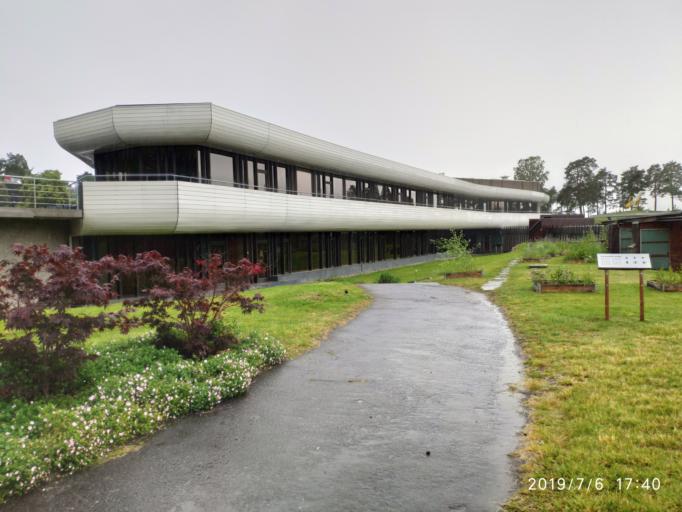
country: NO
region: Akershus
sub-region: Baerum
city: Sandvika
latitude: 59.8895
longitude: 10.5535
